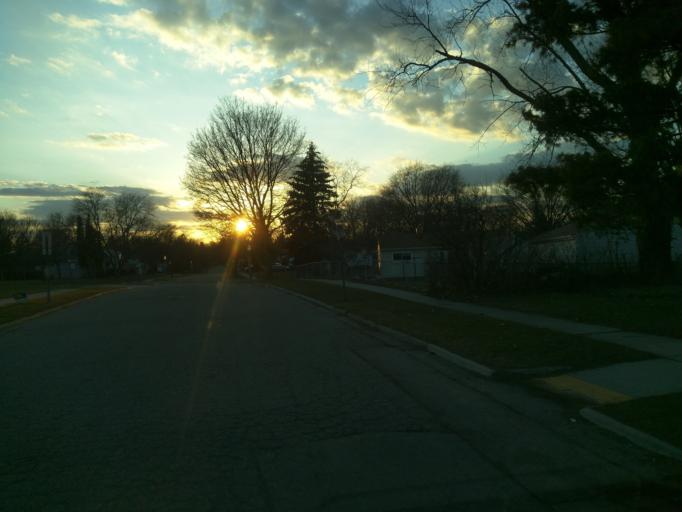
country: US
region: Michigan
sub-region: Ingham County
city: Edgemont Park
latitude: 42.7581
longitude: -84.5878
